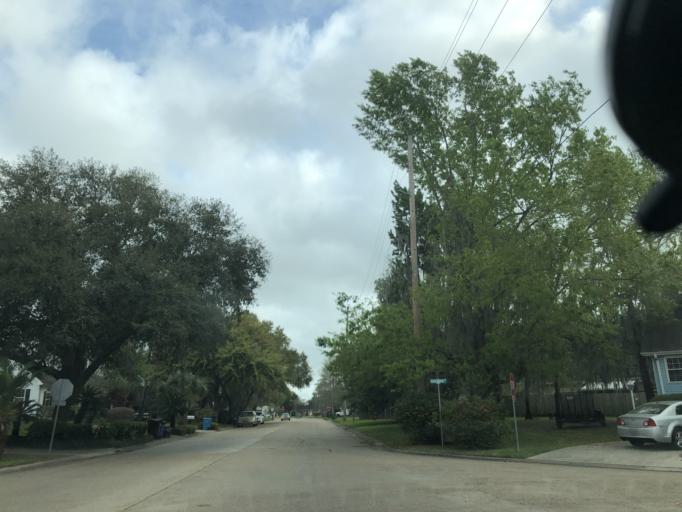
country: US
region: Louisiana
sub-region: Saint Charles Parish
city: New Sarpy
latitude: 29.9673
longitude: -90.3708
